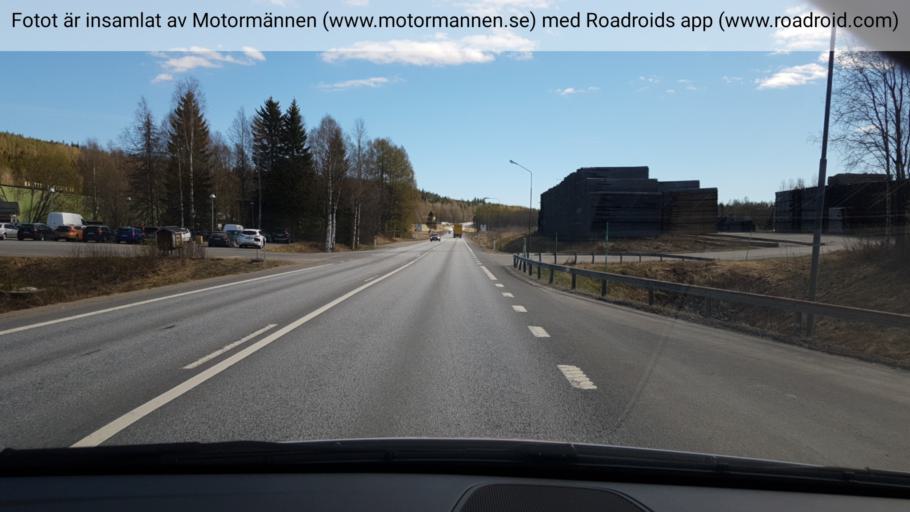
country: SE
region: Vaesterbotten
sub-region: Vannas Kommun
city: Vannasby
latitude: 63.9179
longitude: 19.8748
